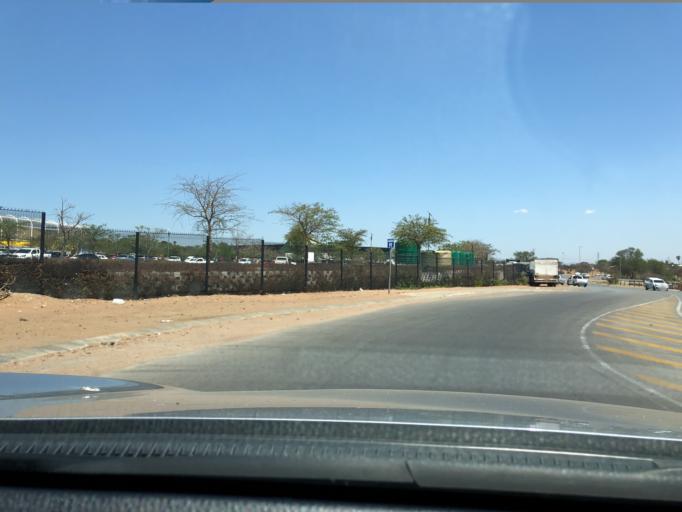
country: ZA
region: Limpopo
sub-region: Capricorn District Municipality
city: Polokwane
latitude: -23.8735
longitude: 29.4645
